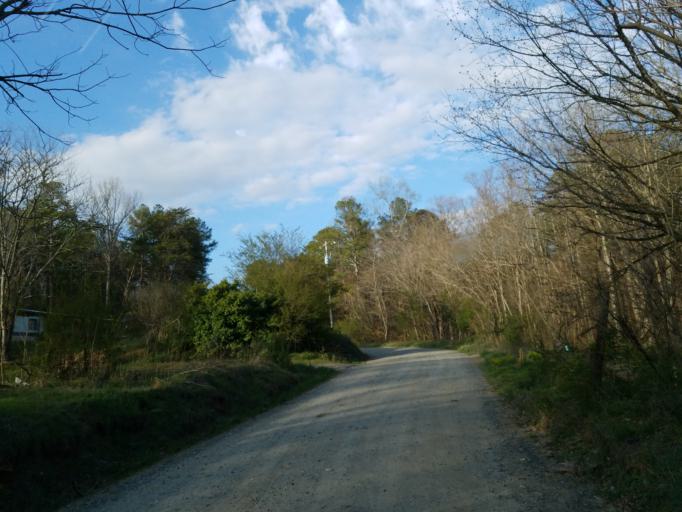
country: US
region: Georgia
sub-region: Bartow County
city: Rydal
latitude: 34.5058
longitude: -84.6318
